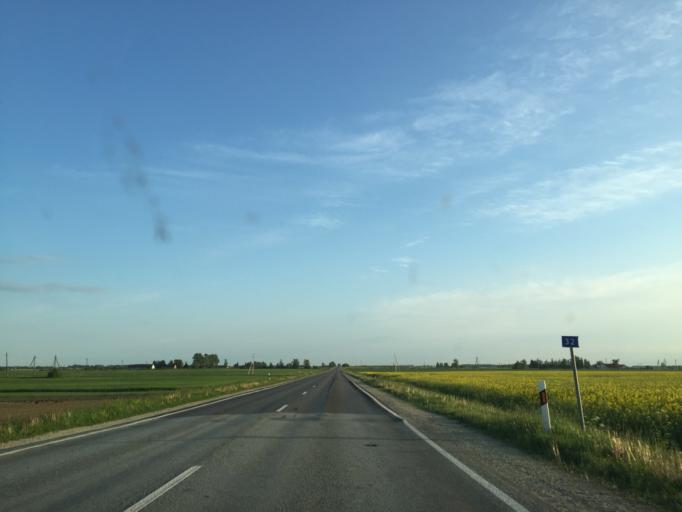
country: LT
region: Siauliu apskritis
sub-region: Joniskis
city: Joniskis
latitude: 56.1019
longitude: 23.4808
